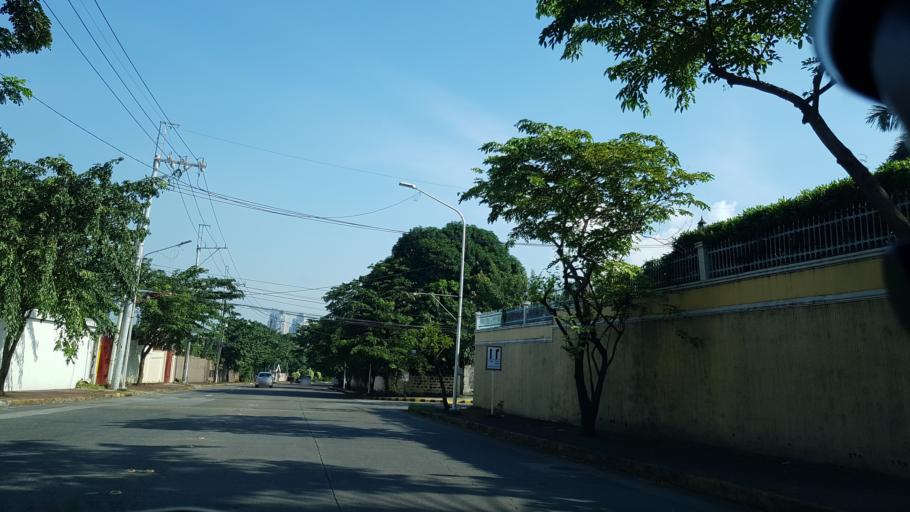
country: PH
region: Metro Manila
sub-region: Pasig
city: Pasig City
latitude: 14.5987
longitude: 121.0713
